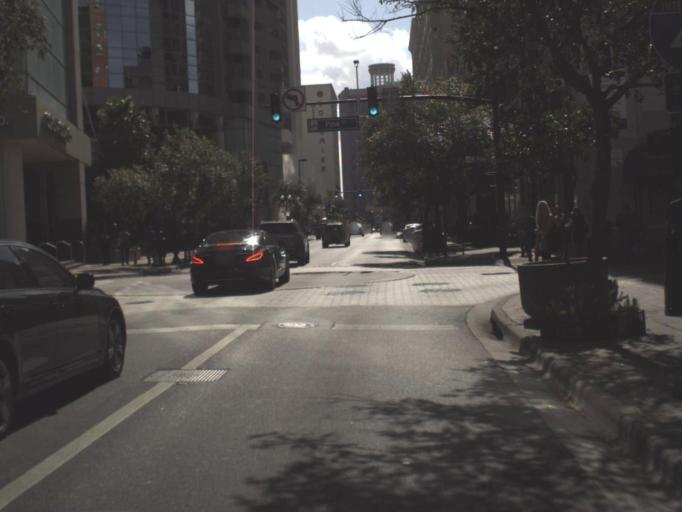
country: US
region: Florida
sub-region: Orange County
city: Orlando
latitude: 28.5415
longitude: -81.3791
